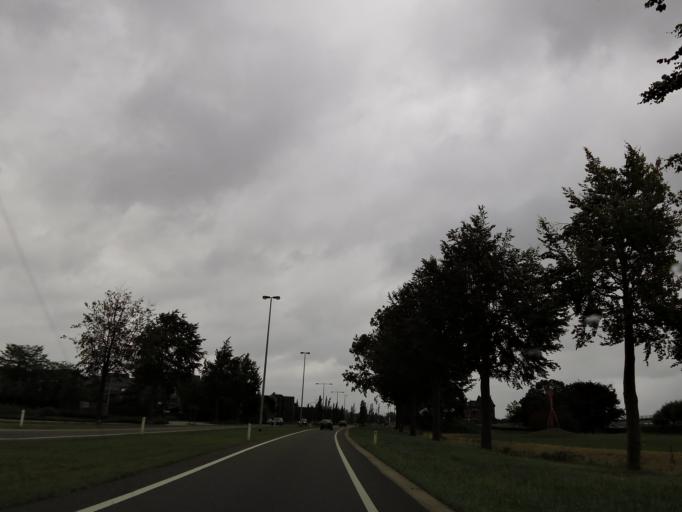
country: BE
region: Flanders
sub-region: Provincie Limburg
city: Maaseik
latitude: 51.0920
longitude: 5.7953
